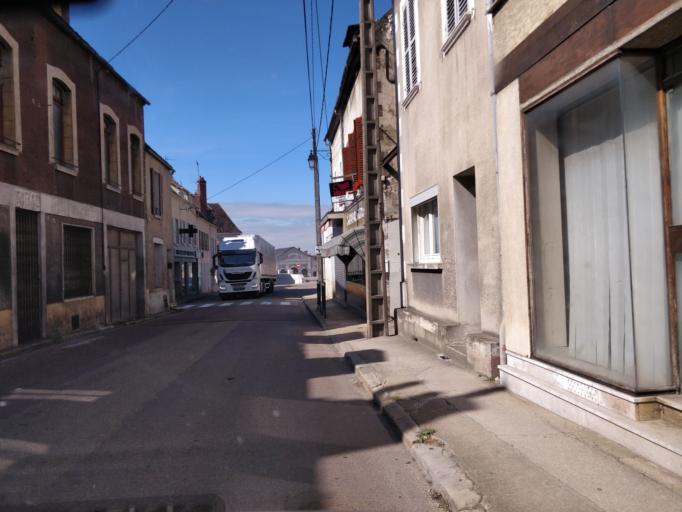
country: FR
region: Bourgogne
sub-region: Departement de l'Yonne
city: Brienon-sur-Armancon
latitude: 47.9929
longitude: 3.6181
